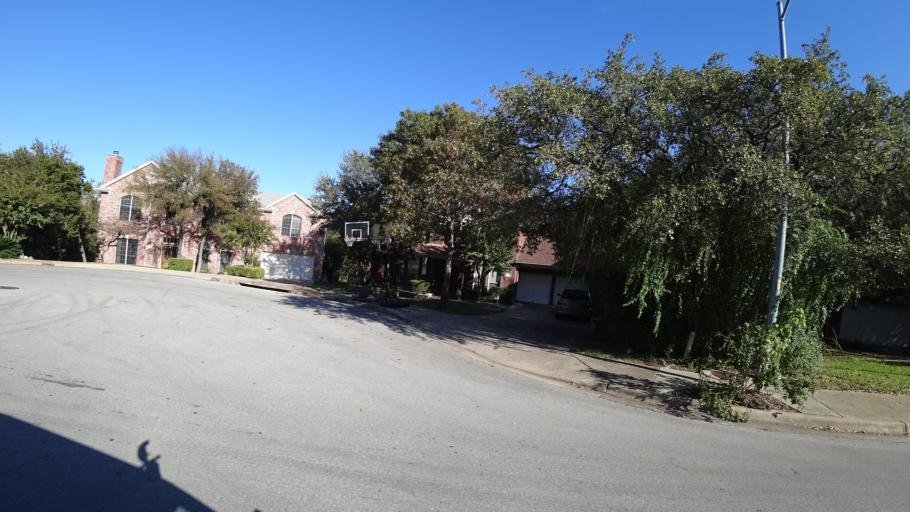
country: US
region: Texas
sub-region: Williamson County
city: Jollyville
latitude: 30.4204
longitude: -97.7778
